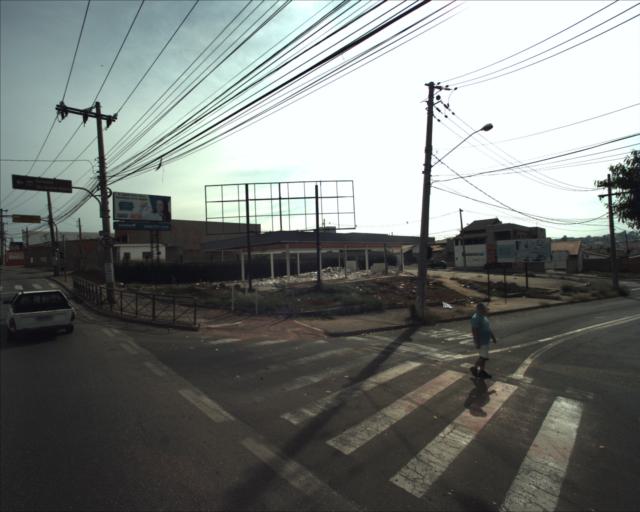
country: BR
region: Sao Paulo
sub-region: Sorocaba
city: Sorocaba
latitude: -23.4673
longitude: -47.4939
